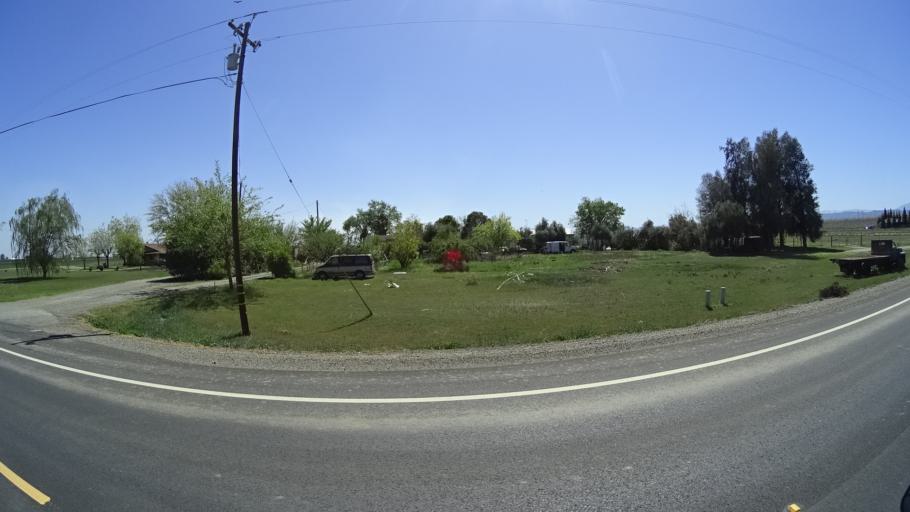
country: US
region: California
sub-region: Glenn County
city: Willows
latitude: 39.5241
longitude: -122.2718
